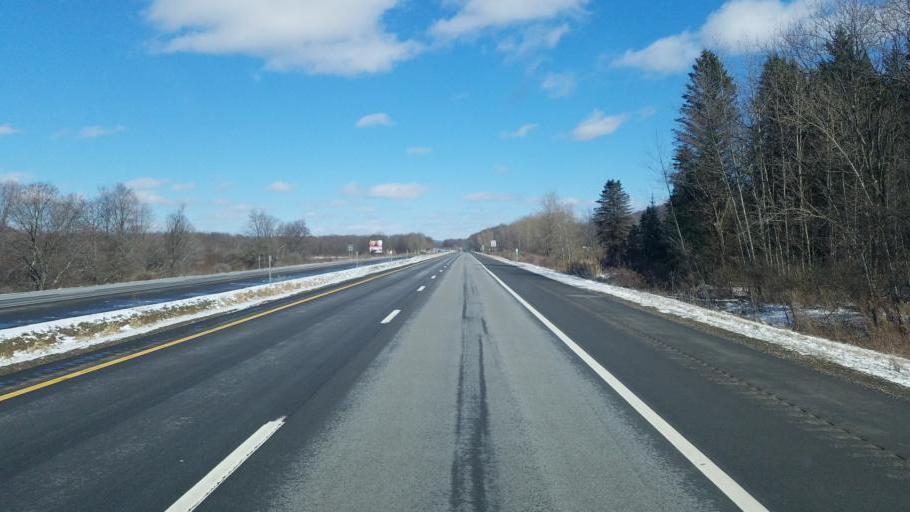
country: US
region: New York
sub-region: Cattaraugus County
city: Allegany
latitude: 42.0858
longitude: -78.5977
